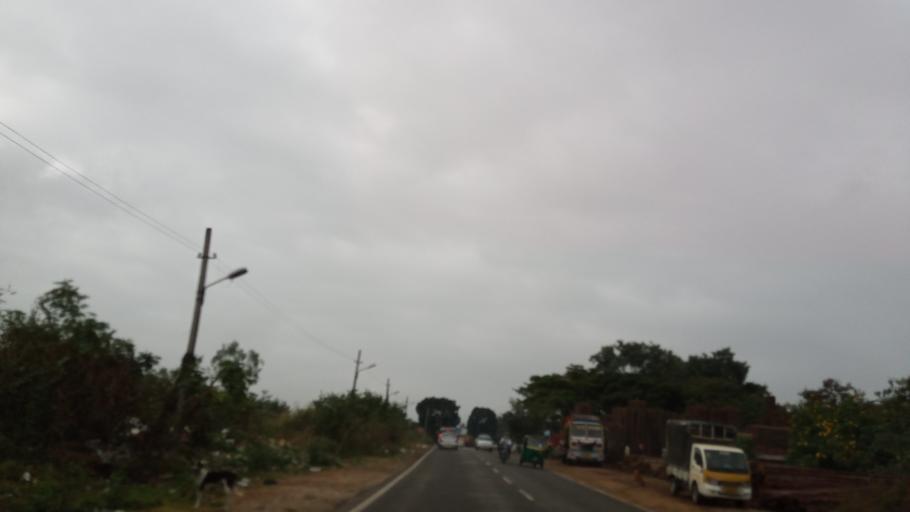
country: IN
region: Karnataka
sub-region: Bangalore Urban
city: Bangalore
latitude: 12.9052
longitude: 77.5324
